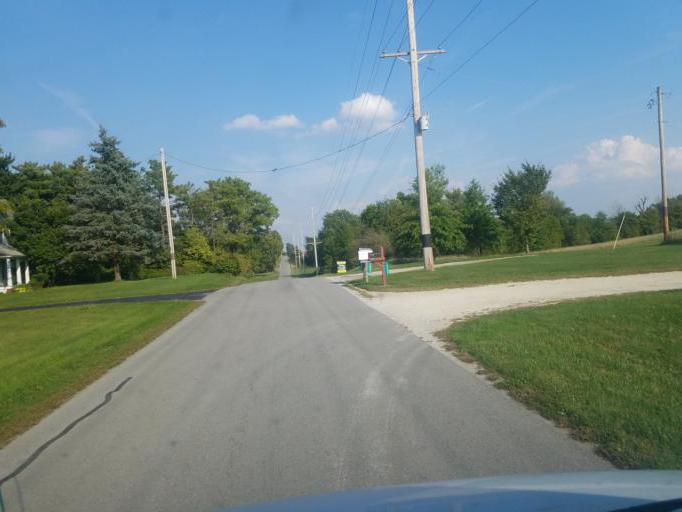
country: US
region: Ohio
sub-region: Wyandot County
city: Carey
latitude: 40.9237
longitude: -83.3168
